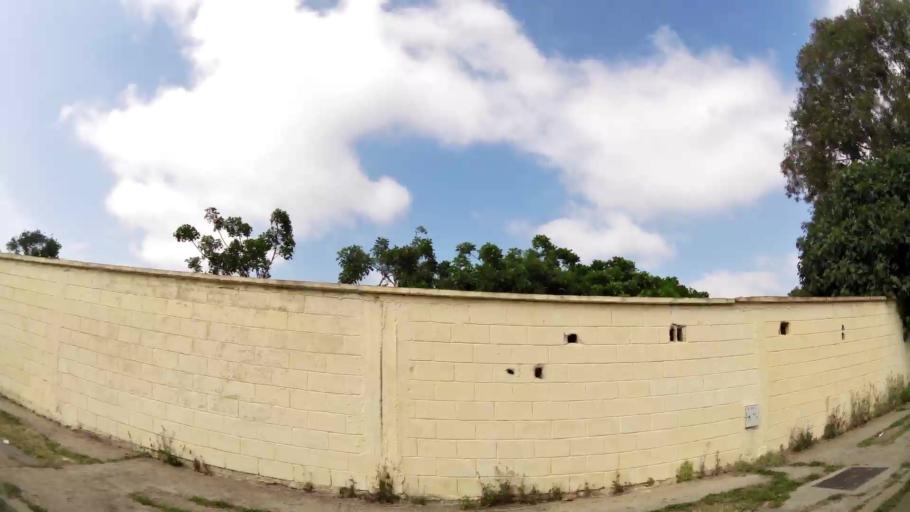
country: MA
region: Rabat-Sale-Zemmour-Zaer
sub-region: Rabat
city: Rabat
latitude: 33.9742
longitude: -6.8530
